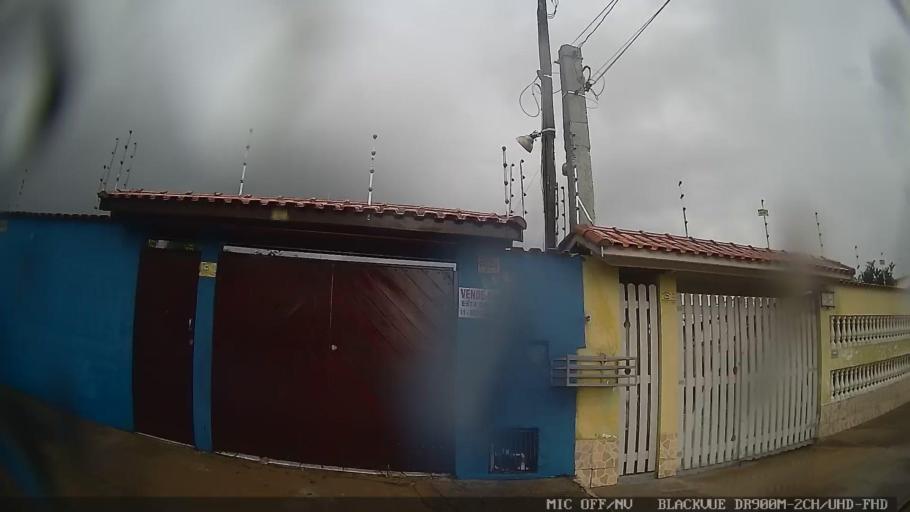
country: BR
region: Sao Paulo
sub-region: Itanhaem
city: Itanhaem
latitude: -24.2366
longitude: -46.9012
